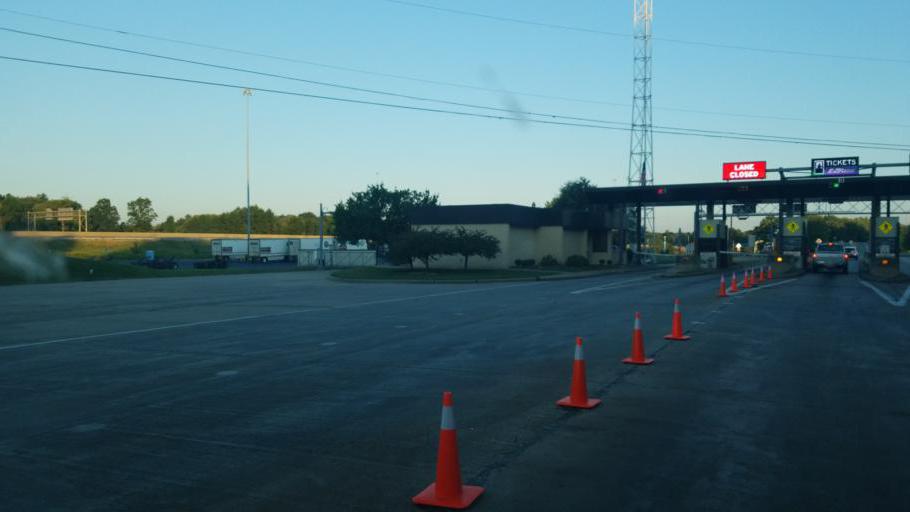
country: US
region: Ohio
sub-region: Trumbull County
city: Newton Falls
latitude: 41.2159
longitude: -80.9541
